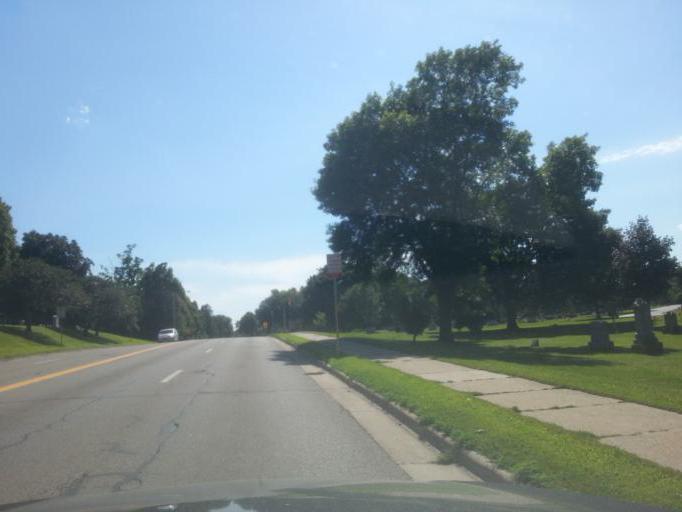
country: US
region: Wisconsin
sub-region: Dane County
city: Shorewood Hills
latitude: 43.0651
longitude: -89.4330
